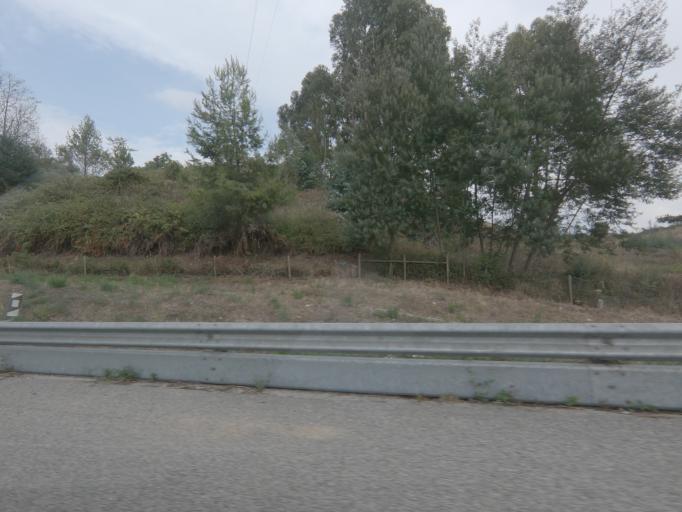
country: PT
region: Coimbra
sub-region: Coimbra
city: Coimbra
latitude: 40.2099
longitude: -8.4463
